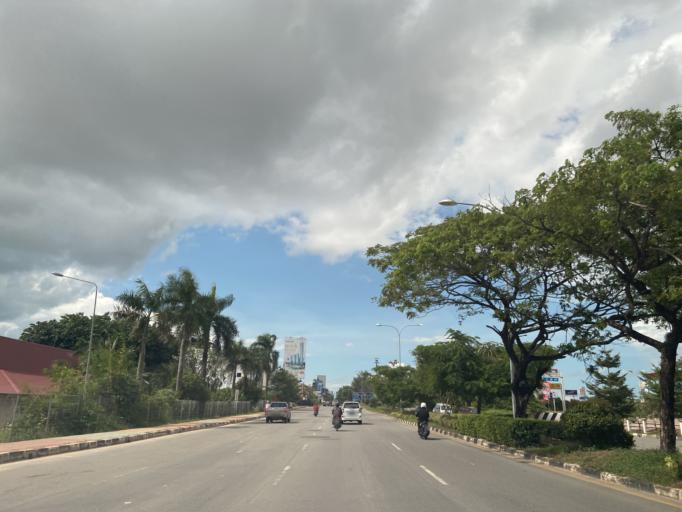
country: SG
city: Singapore
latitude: 1.1330
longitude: 104.0417
